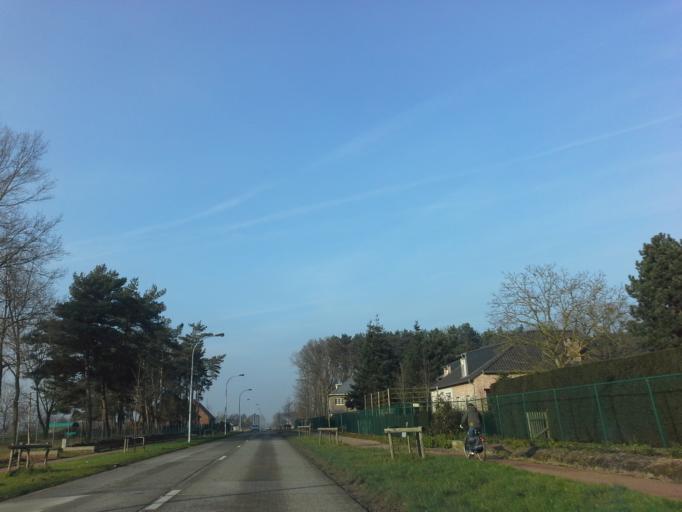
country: BE
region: Flanders
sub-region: Provincie Antwerpen
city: Meerhout
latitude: 51.1522
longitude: 5.0449
